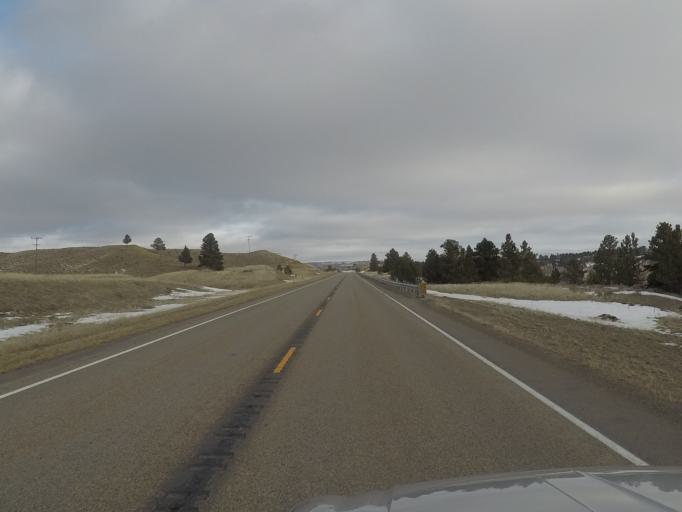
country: US
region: Montana
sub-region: Golden Valley County
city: Ryegate
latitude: 46.3024
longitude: -109.3353
